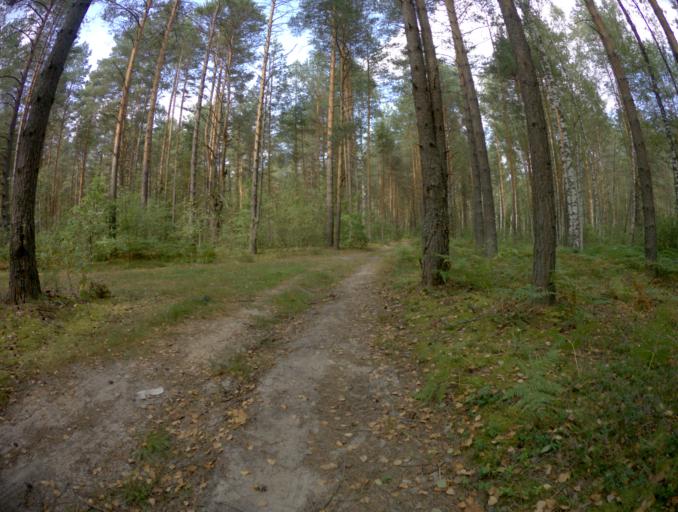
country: RU
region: Vladimir
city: Golovino
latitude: 55.9194
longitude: 40.4872
